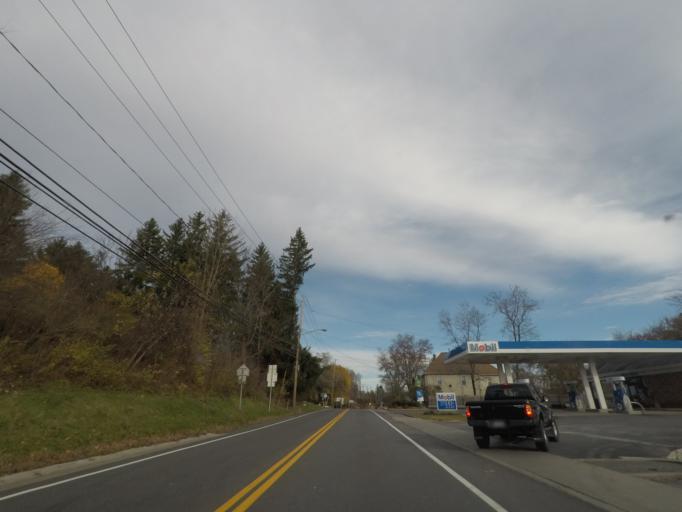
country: US
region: New York
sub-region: Albany County
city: Voorheesville
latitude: 42.6495
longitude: -73.9343
